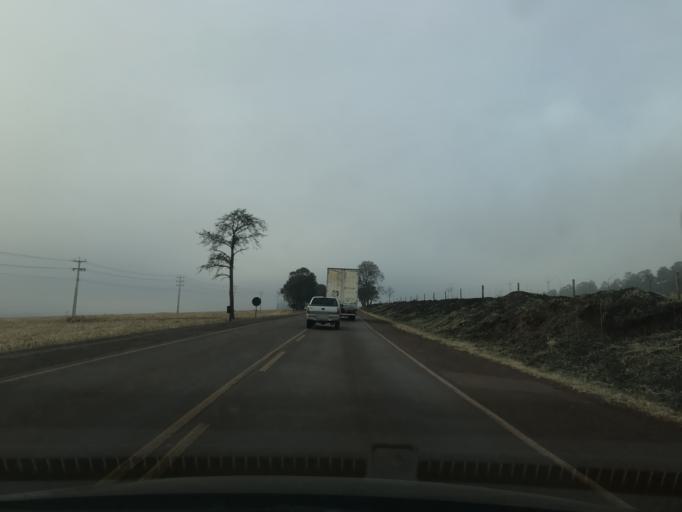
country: BR
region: Parana
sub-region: Toledo
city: Toledo
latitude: -24.6708
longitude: -53.6971
